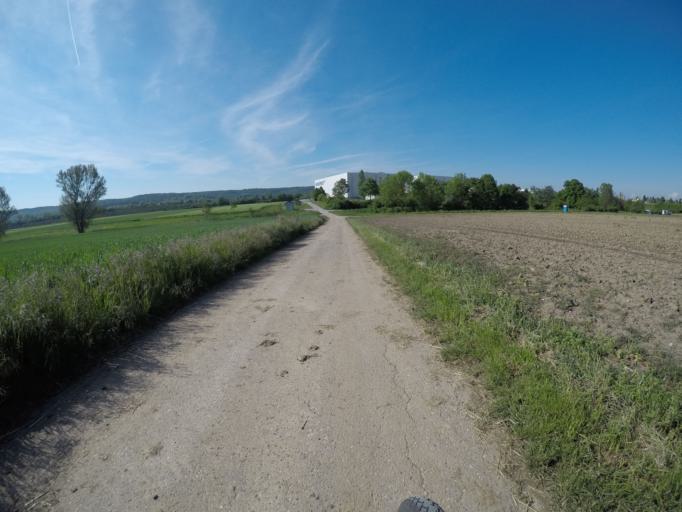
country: DE
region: Baden-Wuerttemberg
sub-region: Regierungsbezirk Stuttgart
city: Gartringen
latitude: 48.6414
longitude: 8.9206
